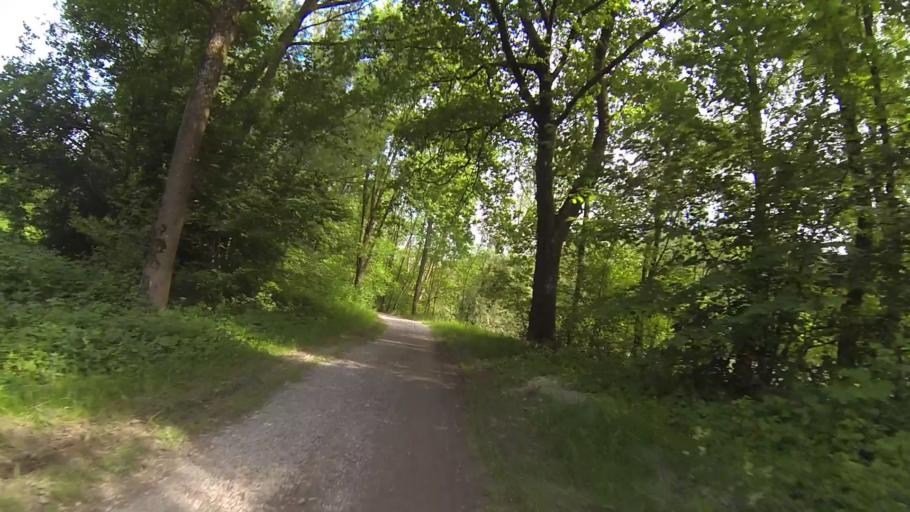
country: DE
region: Bavaria
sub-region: Swabia
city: Senden
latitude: 48.3300
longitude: 10.0188
